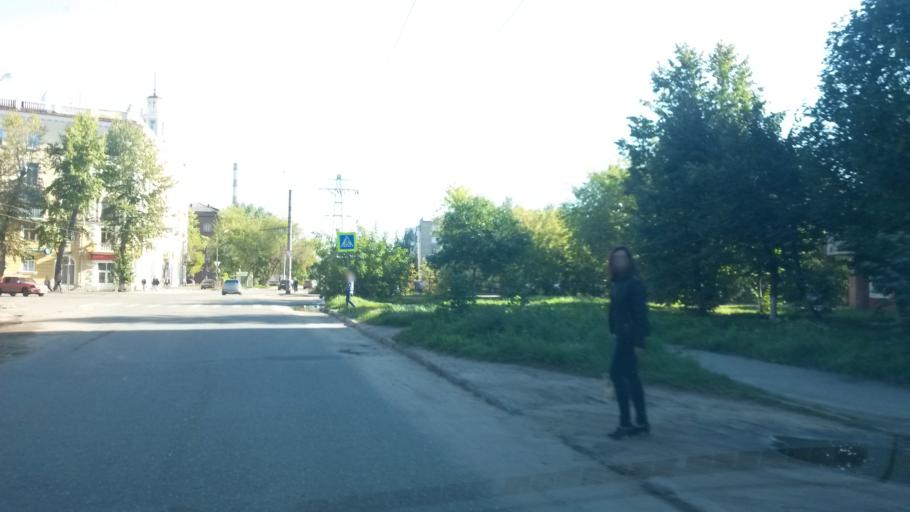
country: RU
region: Ivanovo
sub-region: Gorod Ivanovo
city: Ivanovo
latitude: 56.9997
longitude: 40.9605
